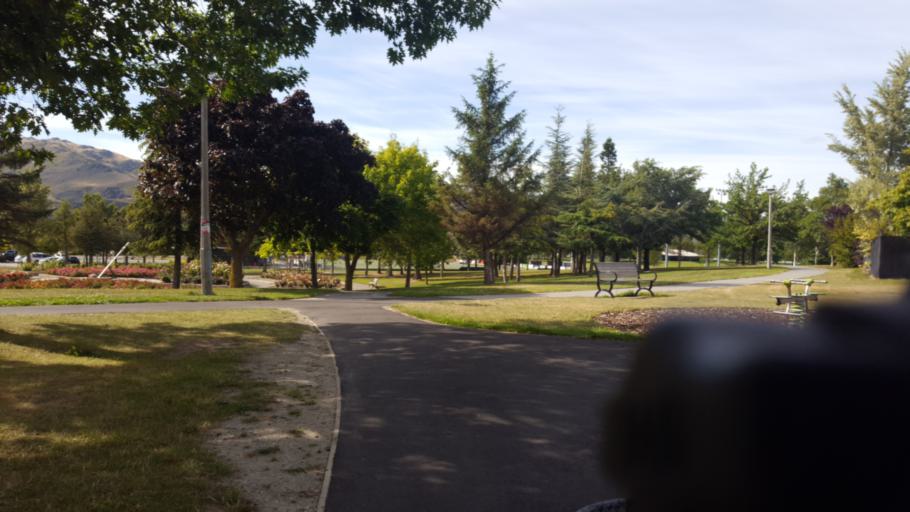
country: NZ
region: Otago
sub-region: Queenstown-Lakes District
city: Wanaka
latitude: -45.0385
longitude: 169.1959
